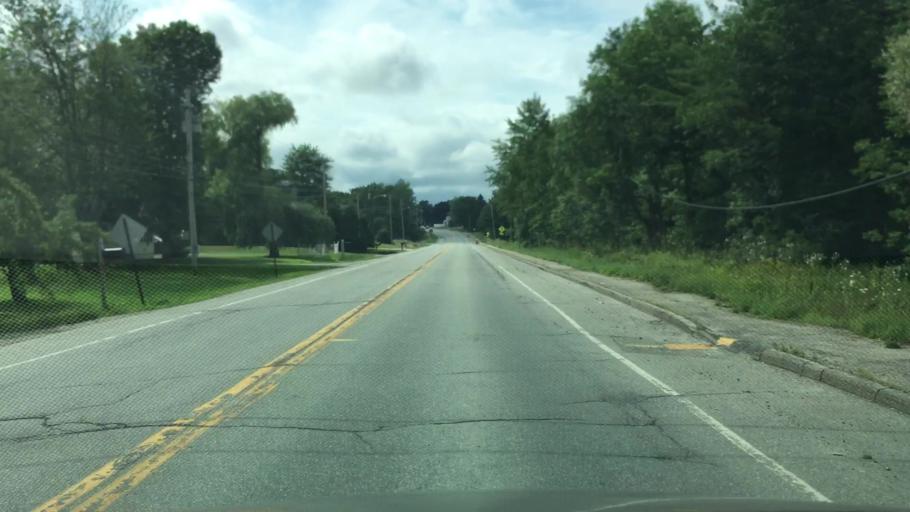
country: US
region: Maine
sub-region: Penobscot County
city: Hampden
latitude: 44.7453
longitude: -68.8489
